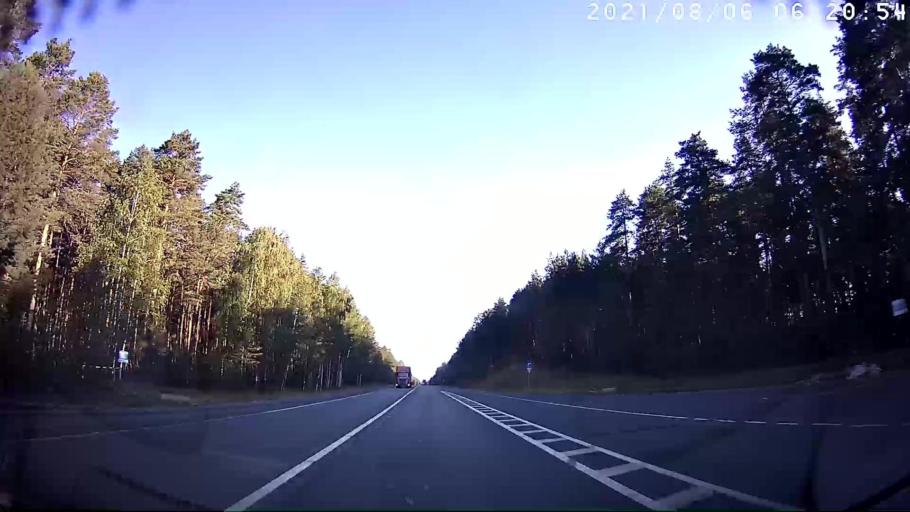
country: RU
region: Mariy-El
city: Pomary
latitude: 56.0609
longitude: 48.3703
